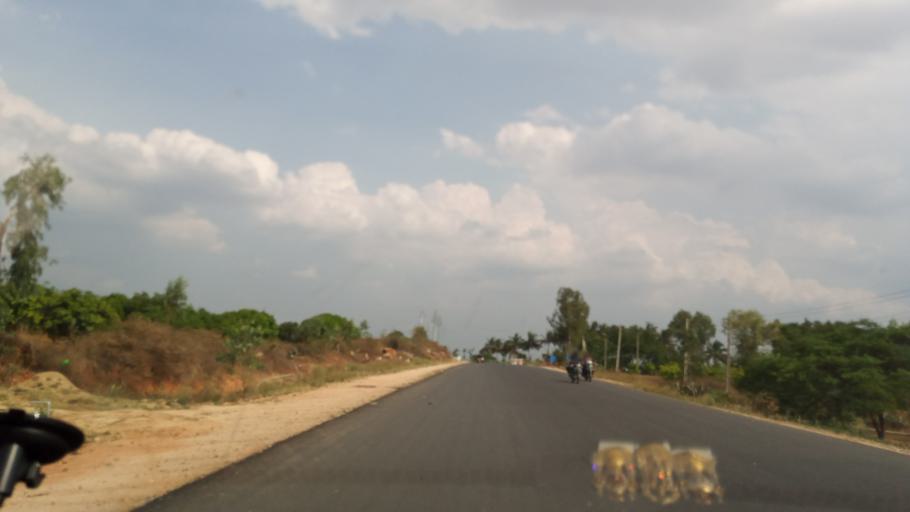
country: IN
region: Tamil Nadu
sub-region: Vellore
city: Peranampattu
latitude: 12.9786
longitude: 78.5085
